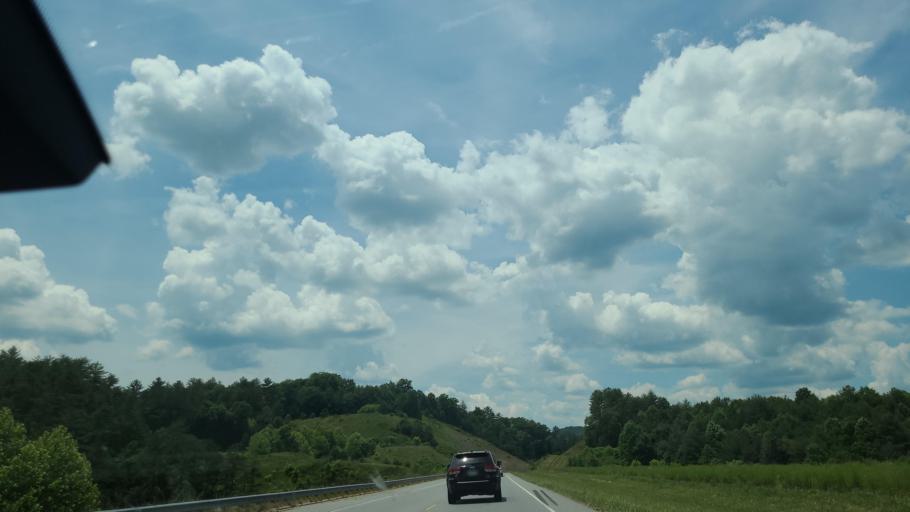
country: US
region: North Carolina
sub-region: Cherokee County
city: Murphy
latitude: 35.0705
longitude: -84.0071
